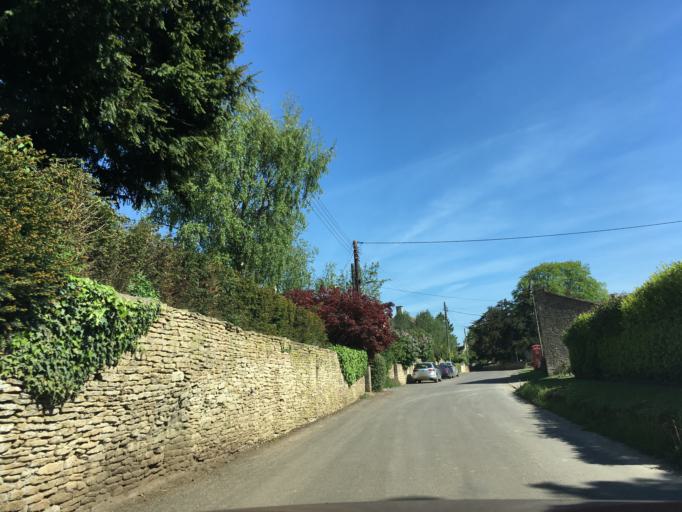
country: GB
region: England
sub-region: Wiltshire
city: Luckington
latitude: 51.6171
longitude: -2.2566
